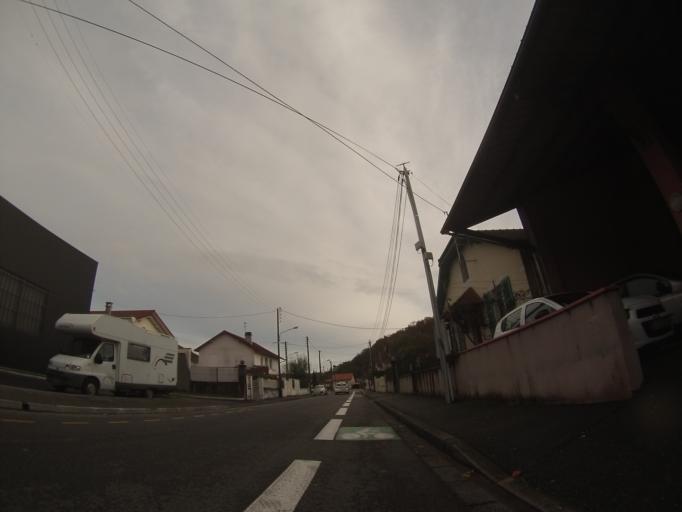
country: FR
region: Aquitaine
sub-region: Departement des Pyrenees-Atlantiques
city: Jurancon
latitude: 43.2830
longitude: -0.3858
